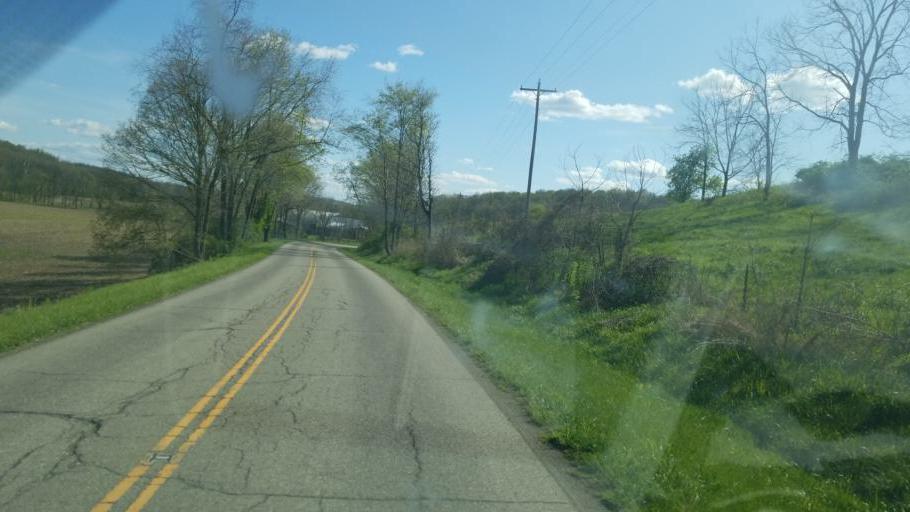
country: US
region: Ohio
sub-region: Coshocton County
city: Coshocton
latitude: 40.3878
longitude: -81.8488
